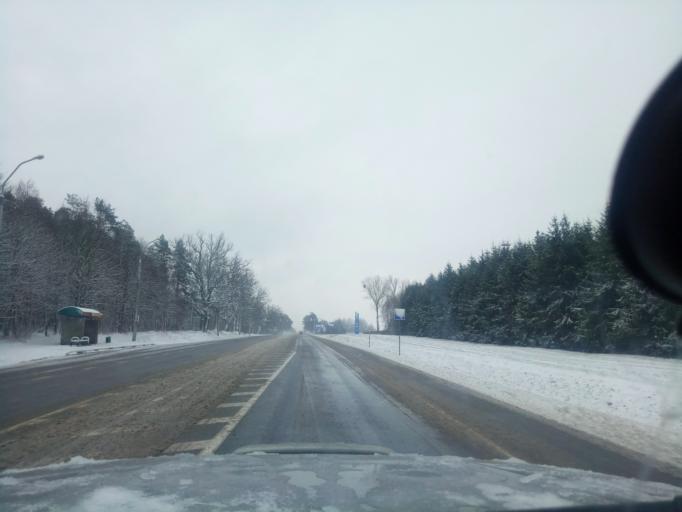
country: BY
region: Minsk
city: Haradzyeya
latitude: 53.2739
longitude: 26.5969
